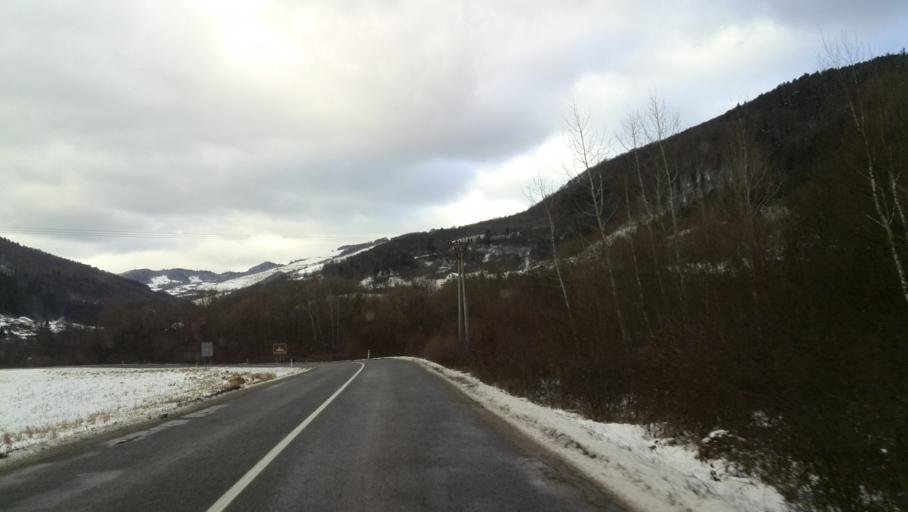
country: SK
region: Kosicky
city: Gelnica
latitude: 48.8680
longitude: 20.9691
